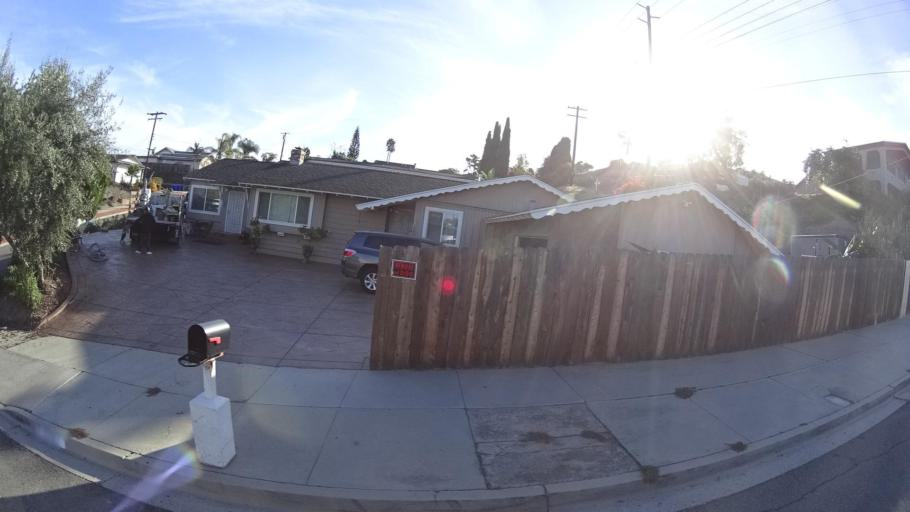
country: US
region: California
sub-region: San Diego County
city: Spring Valley
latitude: 32.7407
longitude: -116.9791
